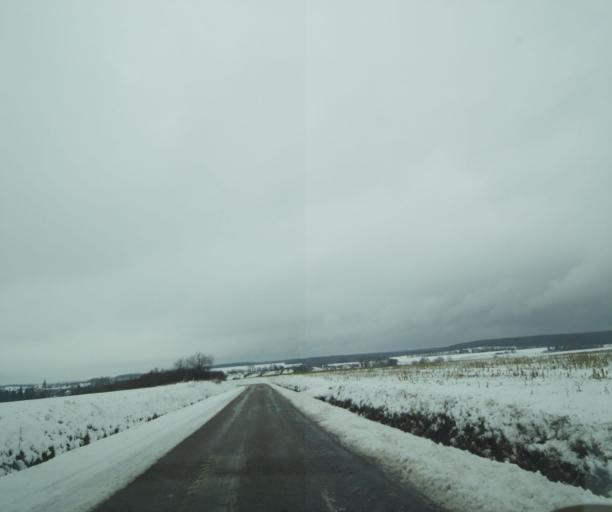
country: FR
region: Champagne-Ardenne
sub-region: Departement de la Haute-Marne
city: Laneuville-a-Remy
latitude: 48.4038
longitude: 4.8532
